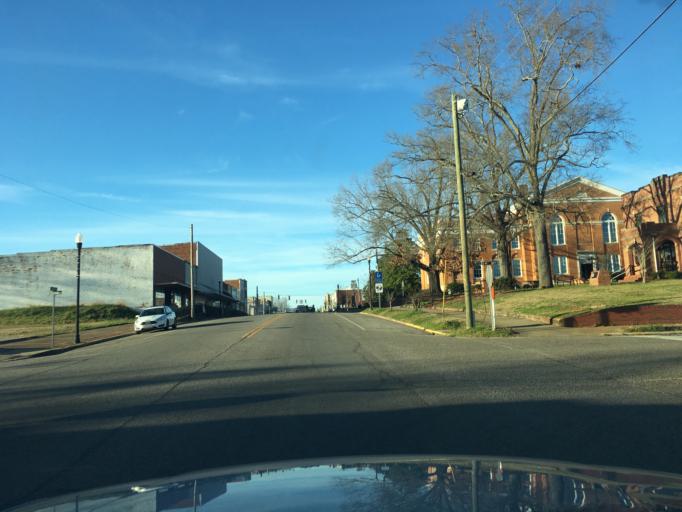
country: US
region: South Carolina
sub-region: Saluda County
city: Saluda
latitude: 34.0002
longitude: -81.7719
